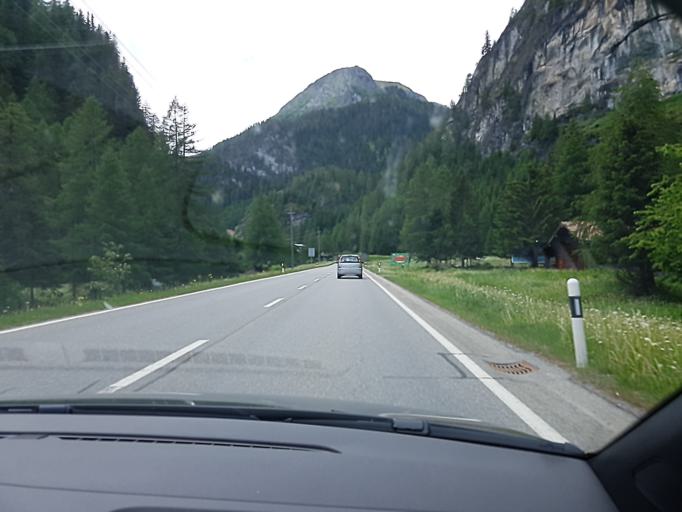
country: CH
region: Grisons
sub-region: Albula District
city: Tiefencastel
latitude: 46.5304
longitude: 9.6215
